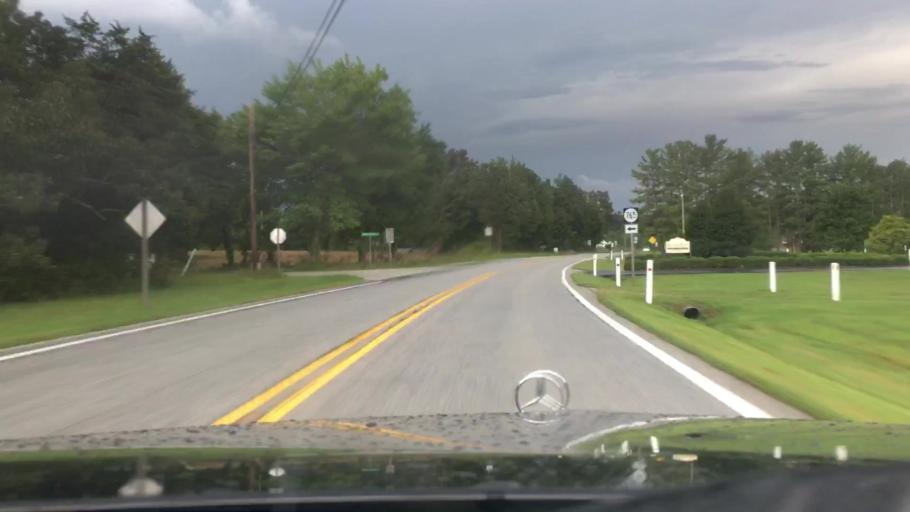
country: US
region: Virginia
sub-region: Nelson County
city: Lovingston
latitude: 37.7626
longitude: -78.9786
